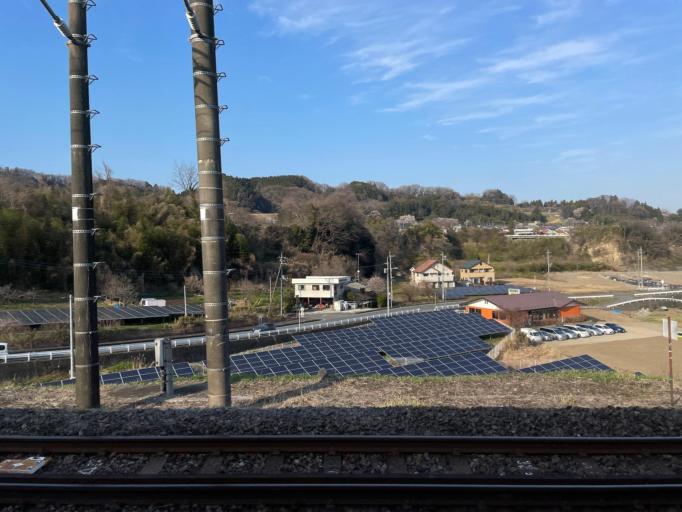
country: JP
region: Gunma
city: Annaka
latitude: 36.3116
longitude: 138.7941
